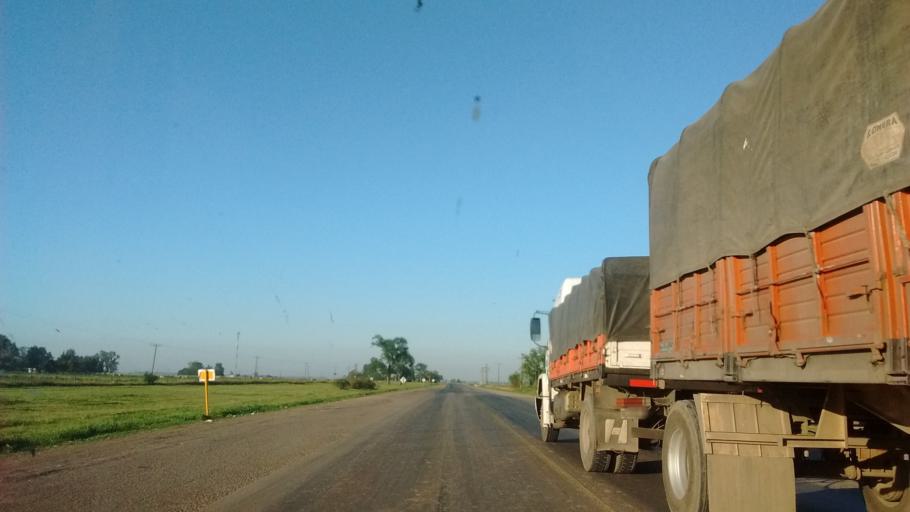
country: AR
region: Santa Fe
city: Firmat
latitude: -33.4614
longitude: -61.5125
